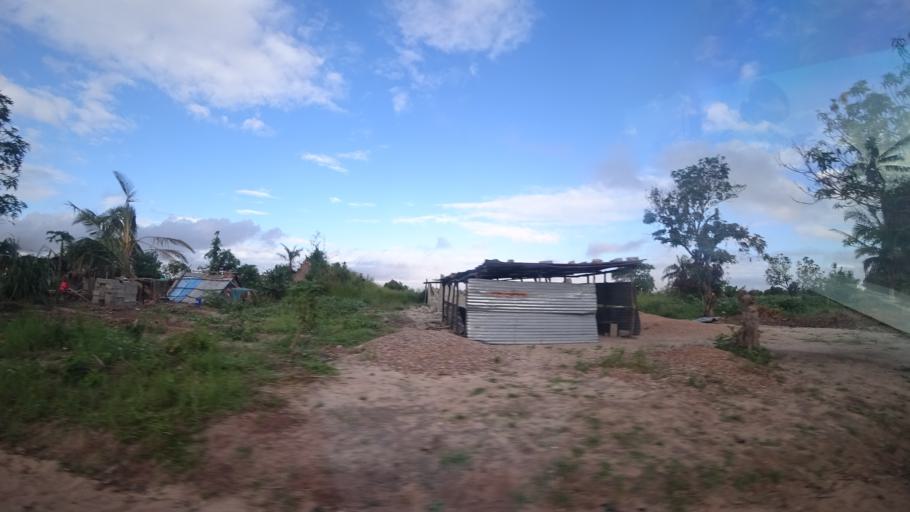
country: MZ
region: Sofala
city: Beira
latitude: -19.6585
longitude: 35.0620
